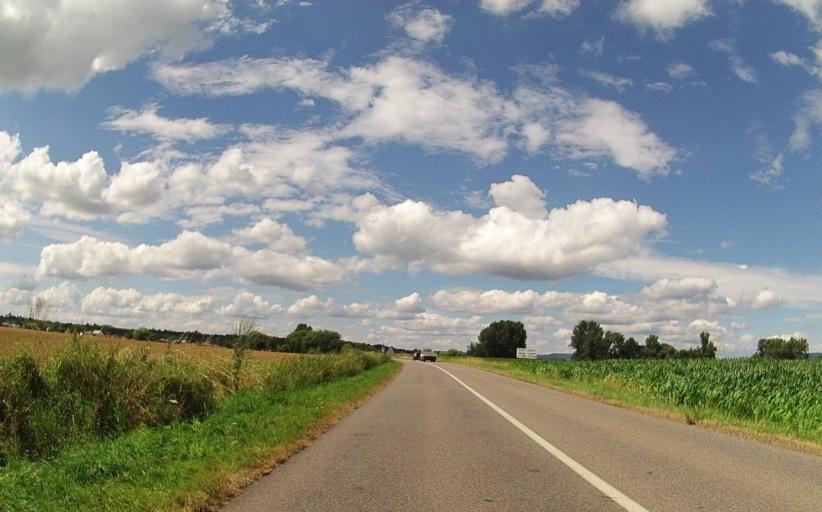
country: FR
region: Alsace
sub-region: Departement du Bas-Rhin
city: Eschbach
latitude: 48.8856
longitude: 7.7512
